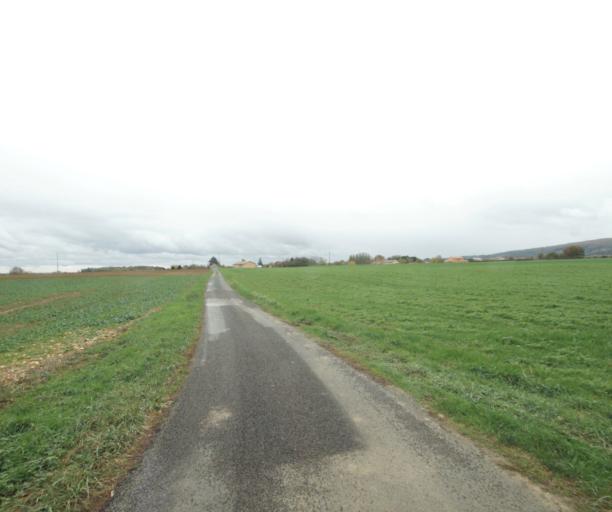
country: FR
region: Rhone-Alpes
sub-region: Departement de l'Ain
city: Pont-de-Vaux
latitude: 46.4683
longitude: 4.8775
